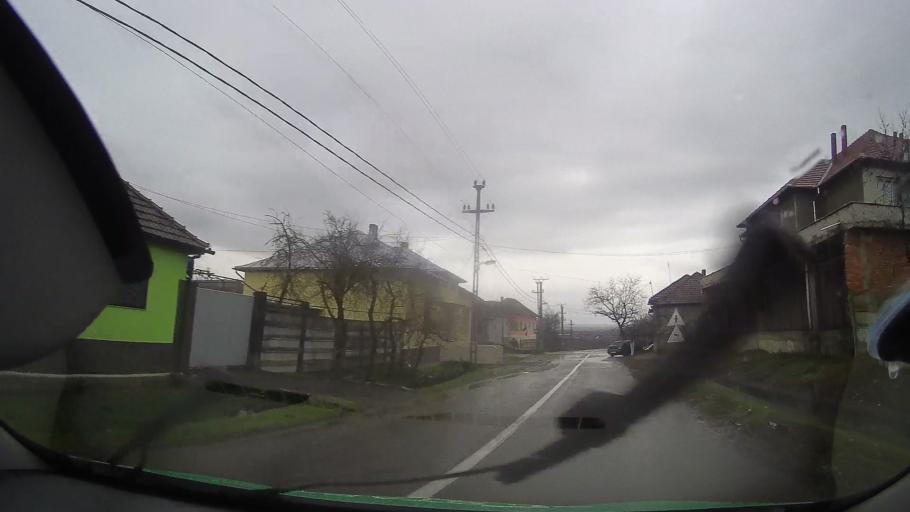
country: RO
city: Capalna
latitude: 46.7360
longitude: 22.1030
